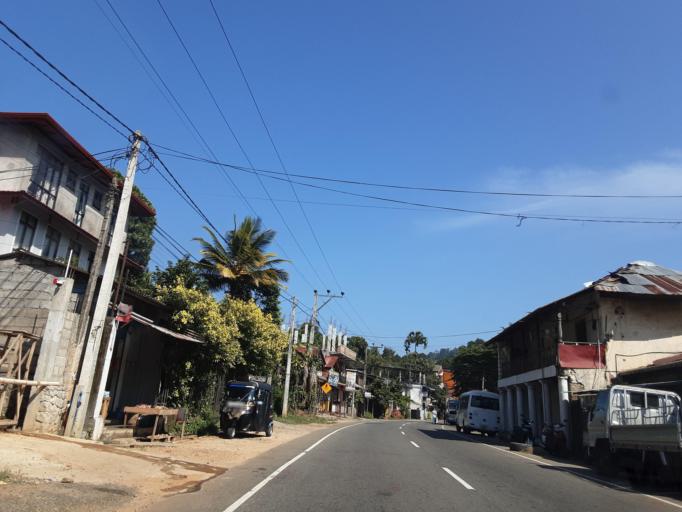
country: LK
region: Uva
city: Badulla
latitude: 7.0004
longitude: 81.0566
